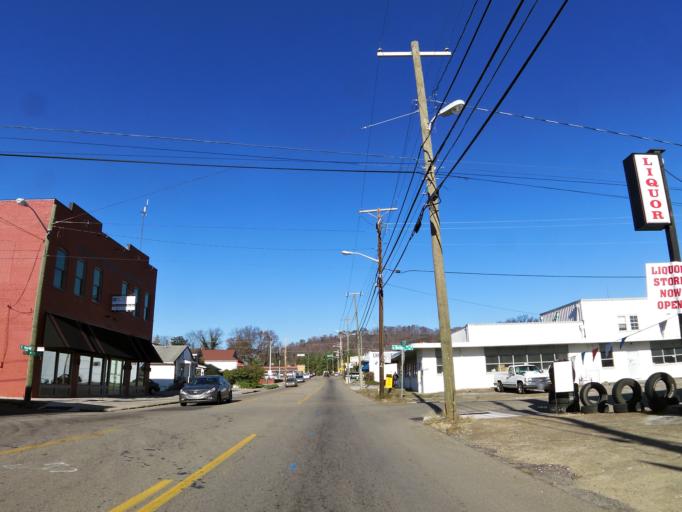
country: US
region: Tennessee
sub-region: Knox County
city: Knoxville
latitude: 35.9906
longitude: -83.9407
